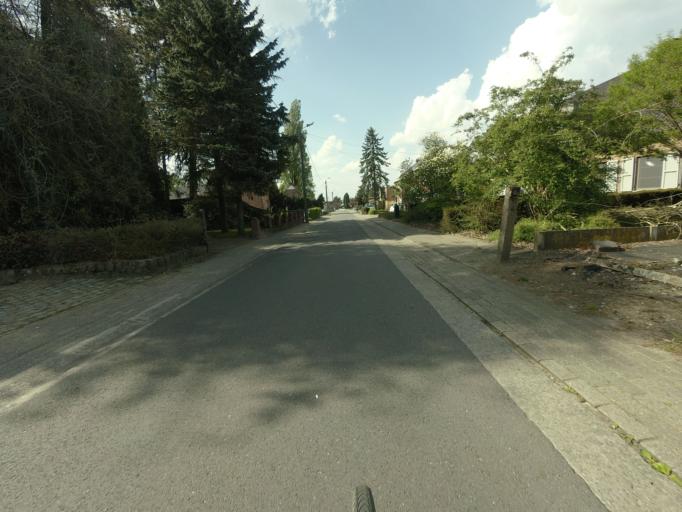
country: BE
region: Flanders
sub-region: Provincie Antwerpen
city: Putte
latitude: 51.0631
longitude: 4.6603
